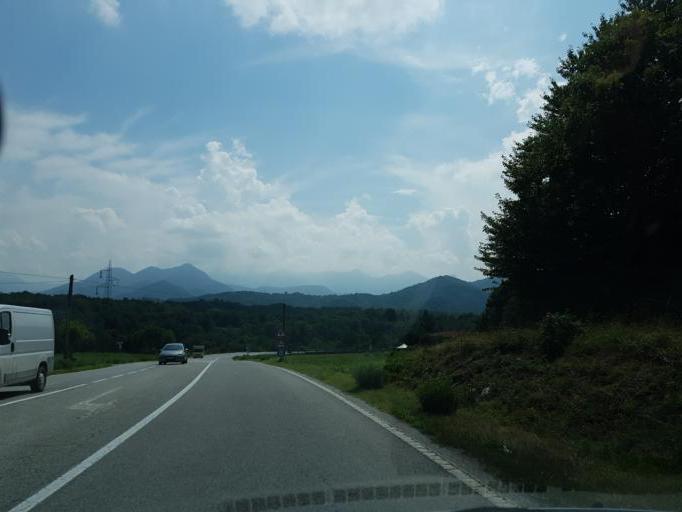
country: IT
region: Piedmont
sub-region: Provincia di Cuneo
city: Vignolo
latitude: 44.3500
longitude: 7.4765
